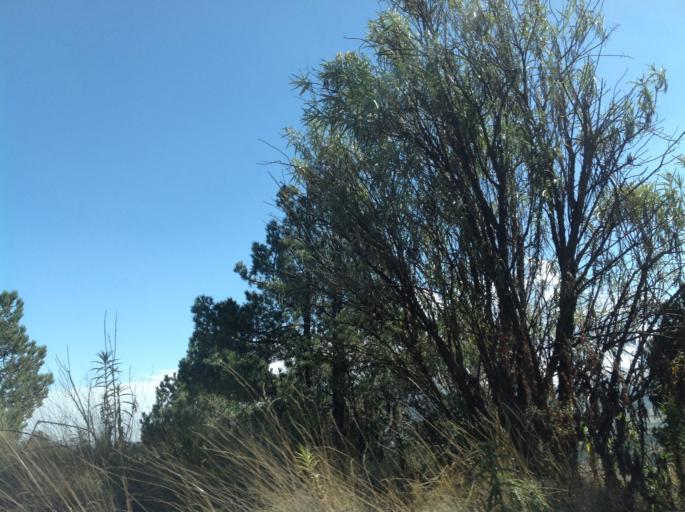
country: MX
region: Mexico
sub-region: Amecameca
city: San Diego Huehuecalco
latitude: 19.0992
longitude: -98.6507
